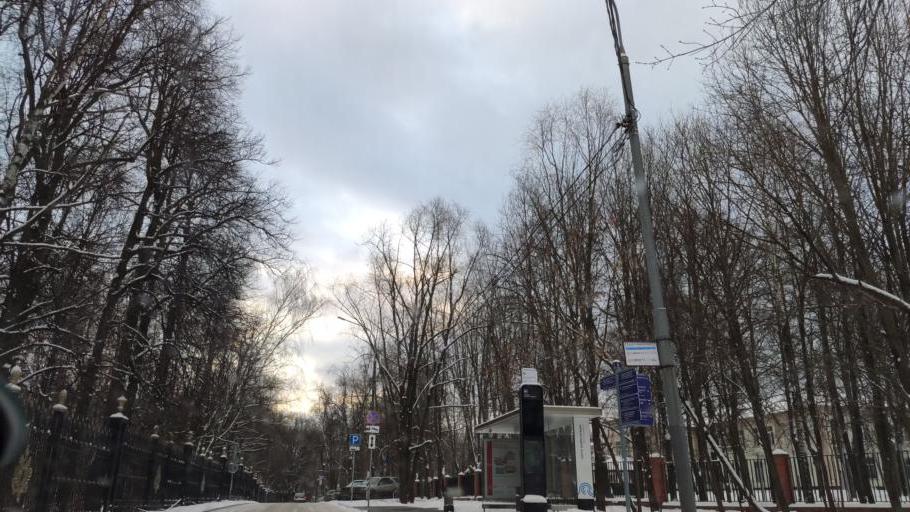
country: RU
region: Moscow
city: Orekhovo-Borisovo Severnoye
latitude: 55.6079
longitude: 37.6761
